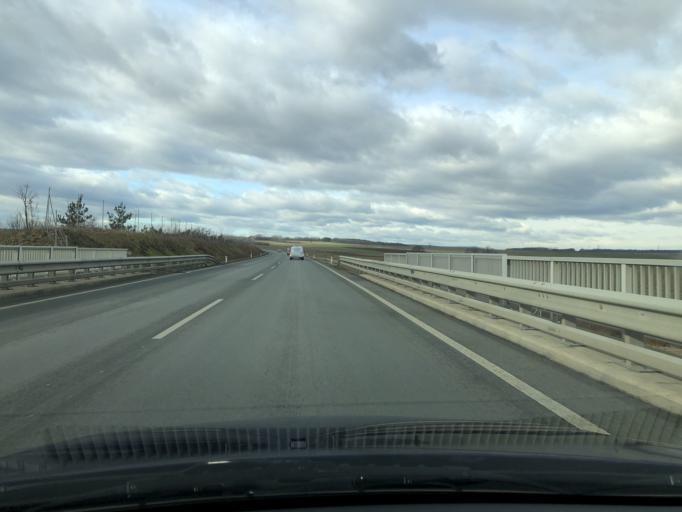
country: AT
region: Burgenland
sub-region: Politischer Bezirk Oberwart
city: Markt Neuhodis
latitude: 47.2758
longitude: 16.4040
